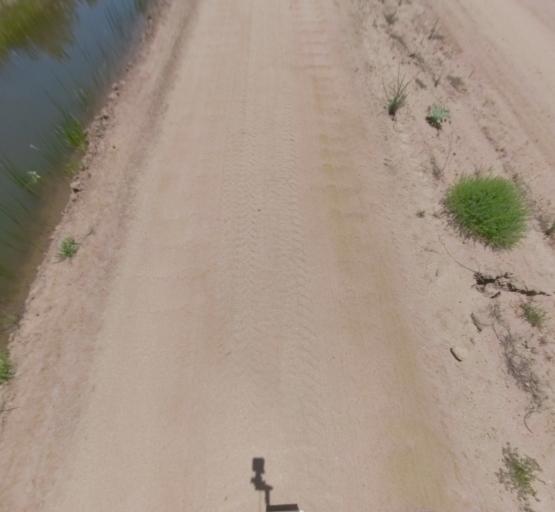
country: US
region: California
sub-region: Madera County
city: Fairmead
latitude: 37.0267
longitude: -120.2295
